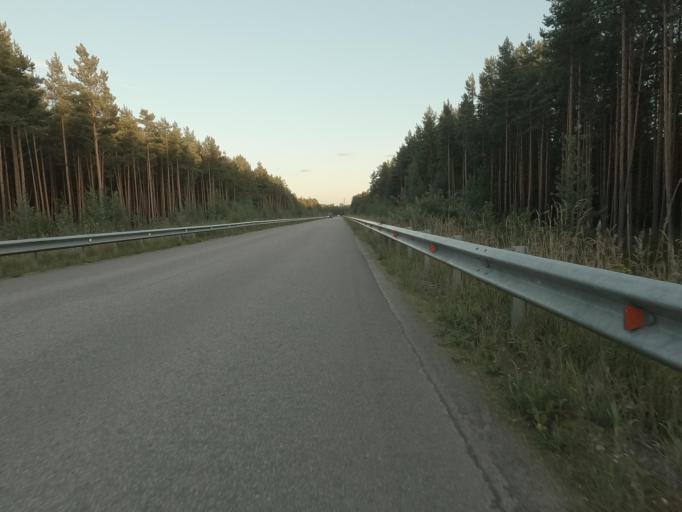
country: RU
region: Leningrad
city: Mga
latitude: 59.7657
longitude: 31.0345
